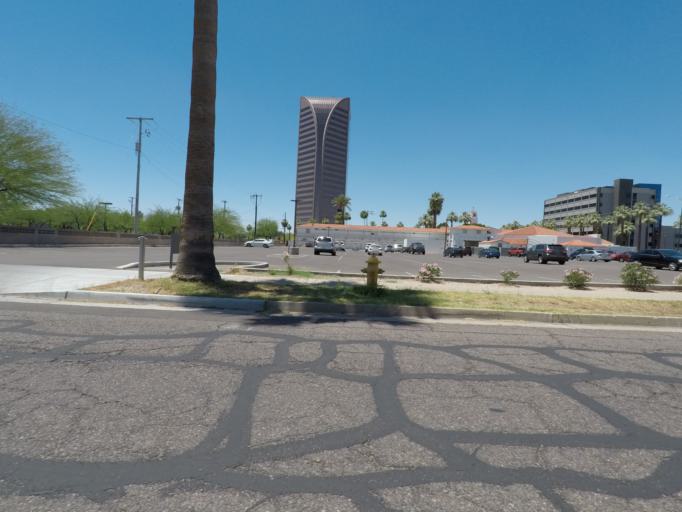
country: US
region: Arizona
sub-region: Maricopa County
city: Phoenix
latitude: 33.4687
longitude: -112.0716
